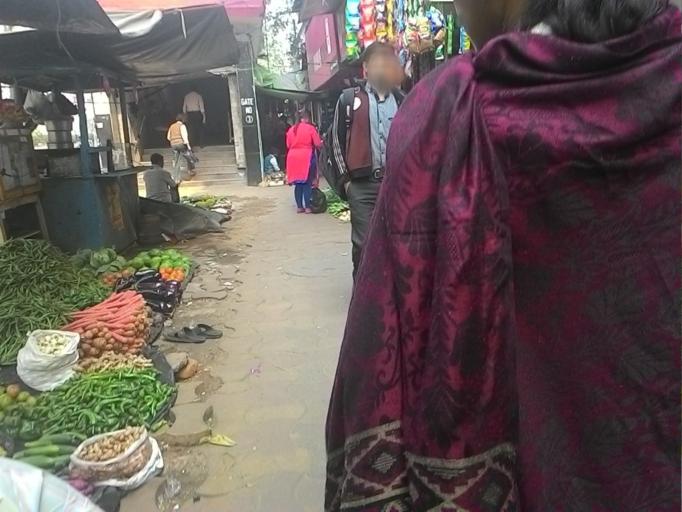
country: IN
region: West Bengal
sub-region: Kolkata
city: Bara Bazar
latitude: 22.5325
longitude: 88.3461
